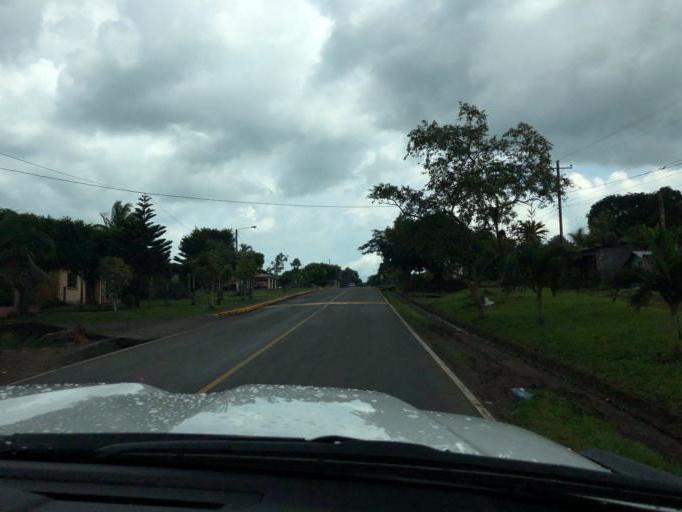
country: NI
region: Chontales
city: Villa Sandino
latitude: 11.9950
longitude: -84.8718
